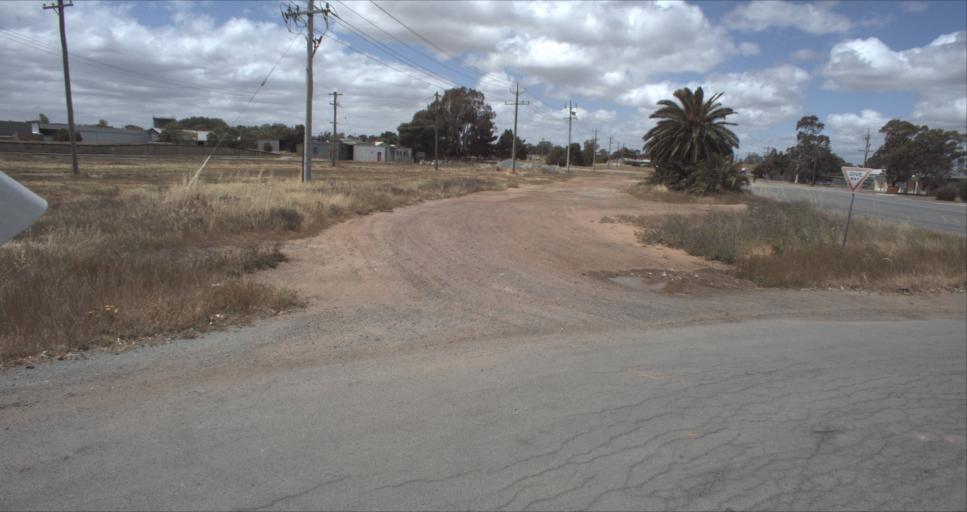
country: AU
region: New South Wales
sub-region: Leeton
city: Leeton
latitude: -34.5539
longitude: 146.3953
